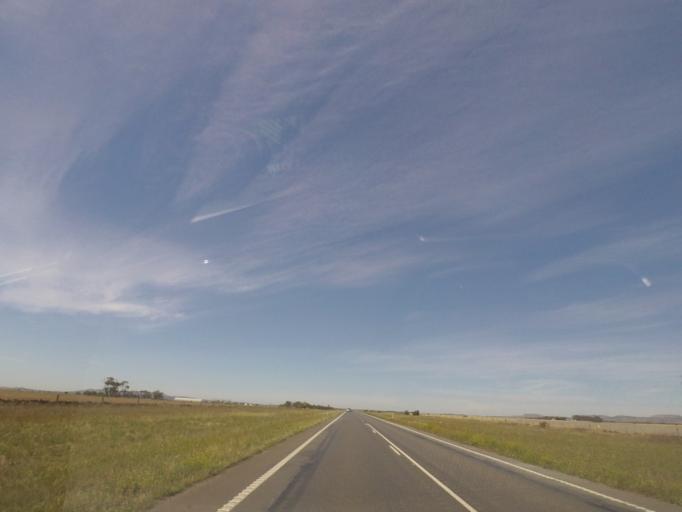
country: AU
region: Victoria
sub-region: Wyndham
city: Wyndham Vale
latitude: -37.8170
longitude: 144.3985
